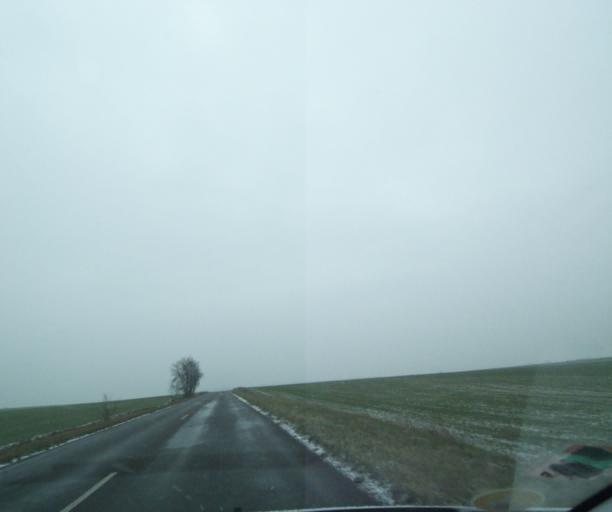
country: FR
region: Champagne-Ardenne
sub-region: Departement de la Haute-Marne
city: Wassy
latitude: 48.4838
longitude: 4.9903
